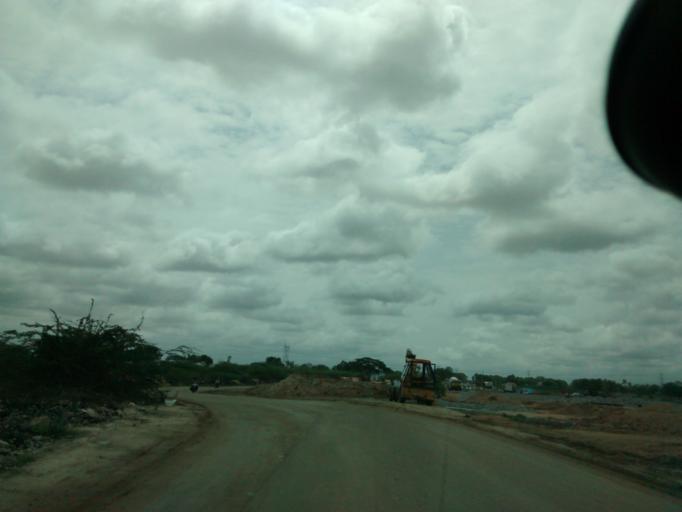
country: IN
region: Andhra Pradesh
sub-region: Anantapur
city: Hindupur
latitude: 13.8117
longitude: 77.5750
